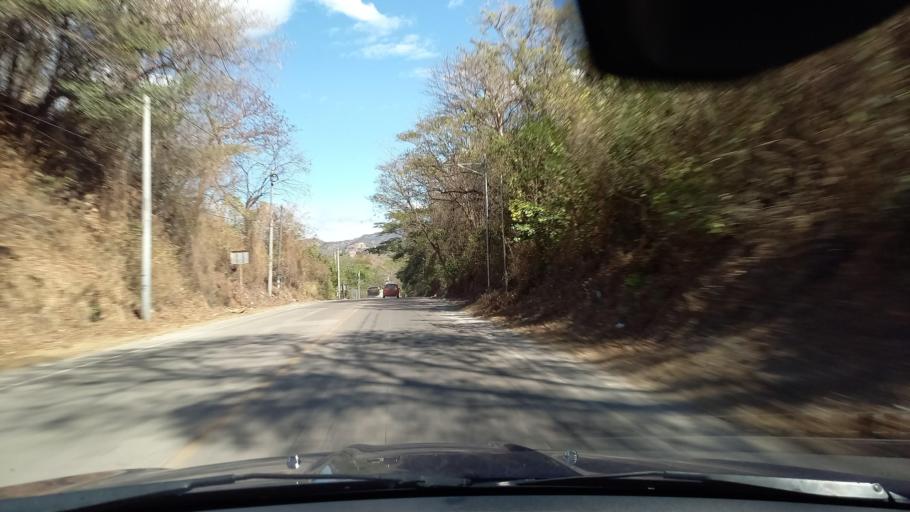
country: SV
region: Santa Ana
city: Metapan
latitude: 14.3458
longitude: -89.4536
